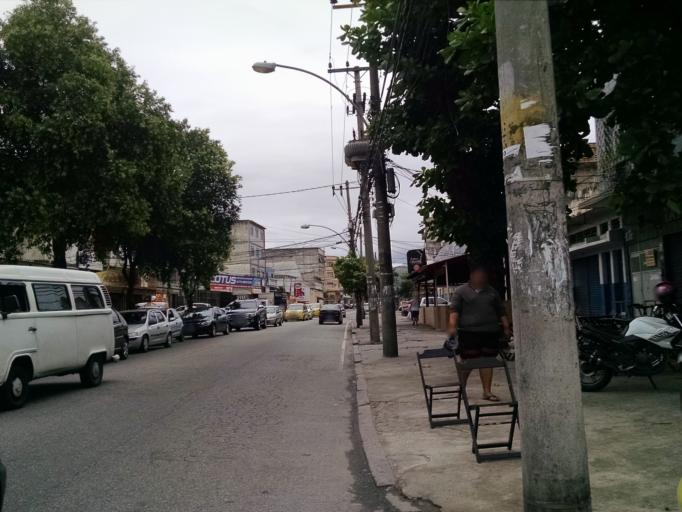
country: BR
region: Rio de Janeiro
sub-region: Duque De Caxias
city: Duque de Caxias
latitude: -22.8293
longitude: -43.3193
